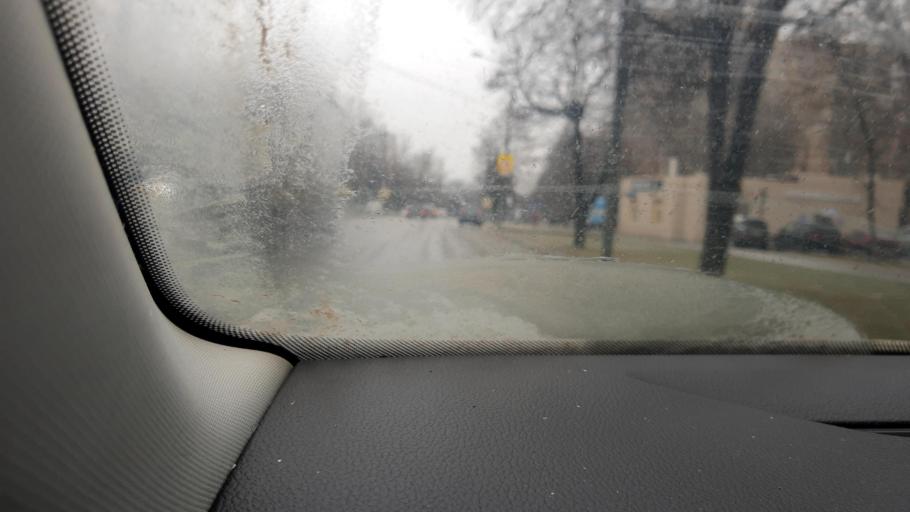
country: RU
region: Moscow
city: Tsaritsyno
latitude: 55.6292
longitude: 37.6555
